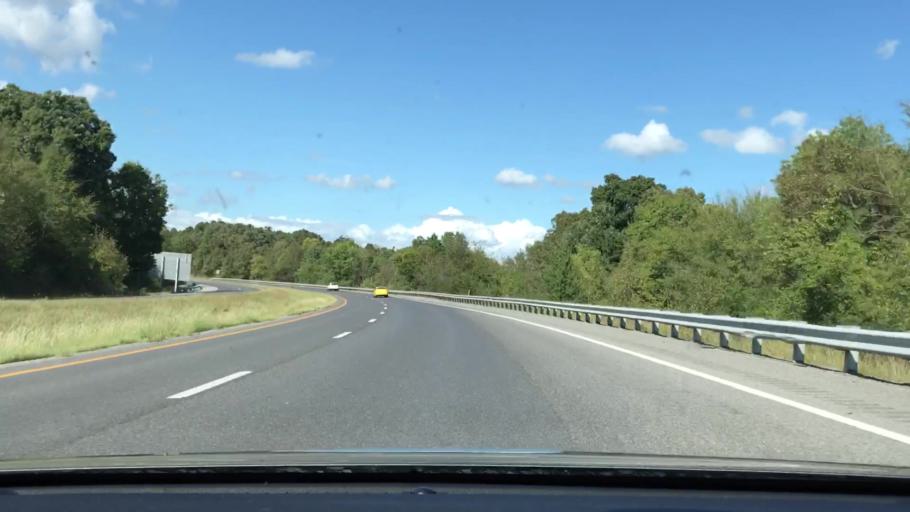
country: US
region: Kentucky
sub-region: Marshall County
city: Benton
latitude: 36.9327
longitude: -88.3429
